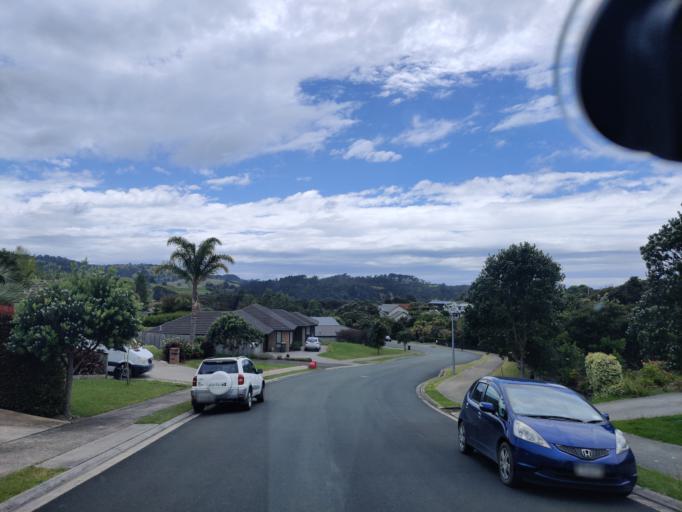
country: NZ
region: Auckland
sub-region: Auckland
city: Rothesay Bay
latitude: -36.5675
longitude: 174.6867
